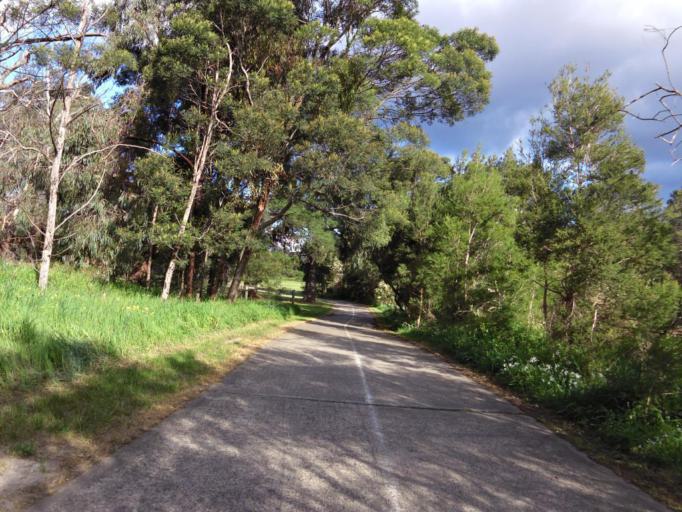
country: AU
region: Victoria
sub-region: Manningham
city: Doncaster East
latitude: -37.7983
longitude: 145.1458
